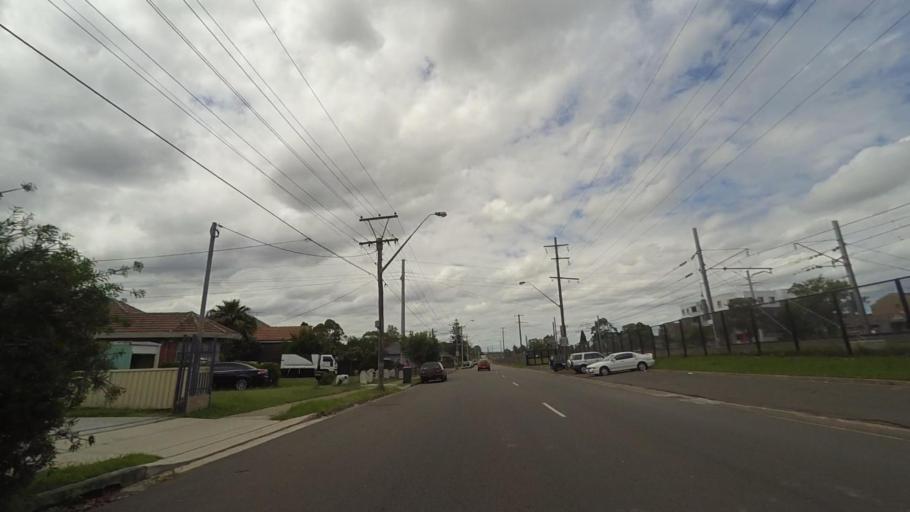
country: AU
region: New South Wales
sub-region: Holroyd
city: Guildford West
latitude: -33.8522
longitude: 150.9857
